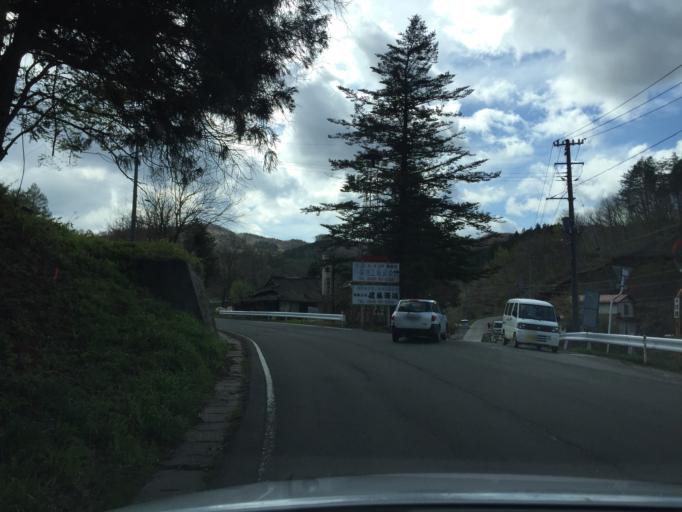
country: JP
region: Fukushima
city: Funehikimachi-funehiki
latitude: 37.5863
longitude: 140.6920
